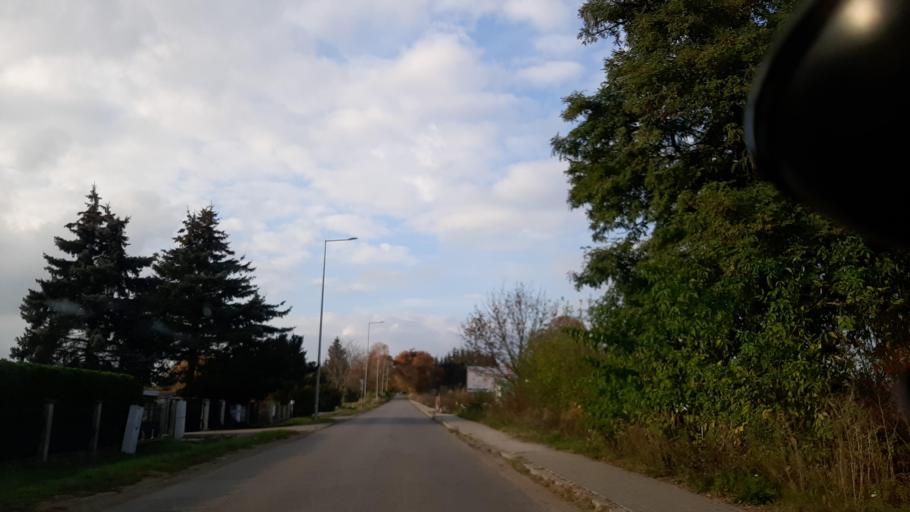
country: PL
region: Lublin Voivodeship
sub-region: Powiat pulawski
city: Naleczow
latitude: 51.3090
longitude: 22.2188
